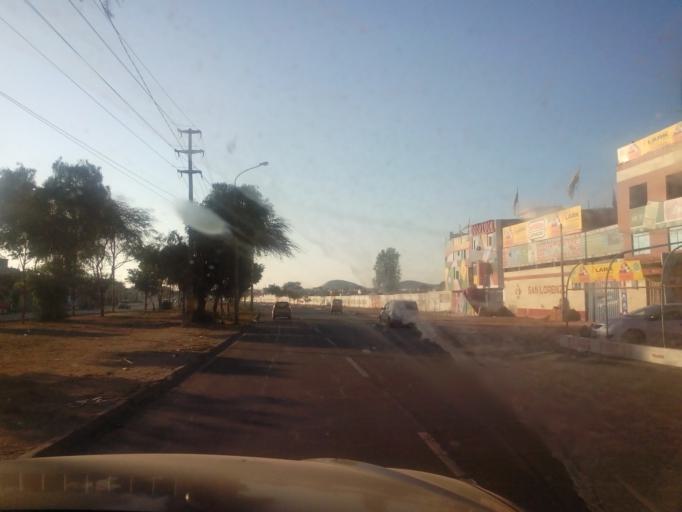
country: PE
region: Ica
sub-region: Provincia de Ica
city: Ica
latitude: -14.0597
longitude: -75.7419
